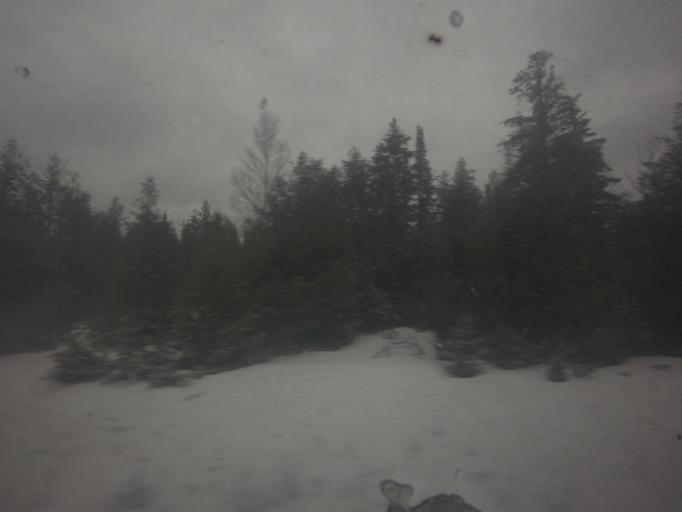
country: CA
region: Ontario
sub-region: Lanark County
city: Smiths Falls
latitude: 45.0400
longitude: -75.9258
